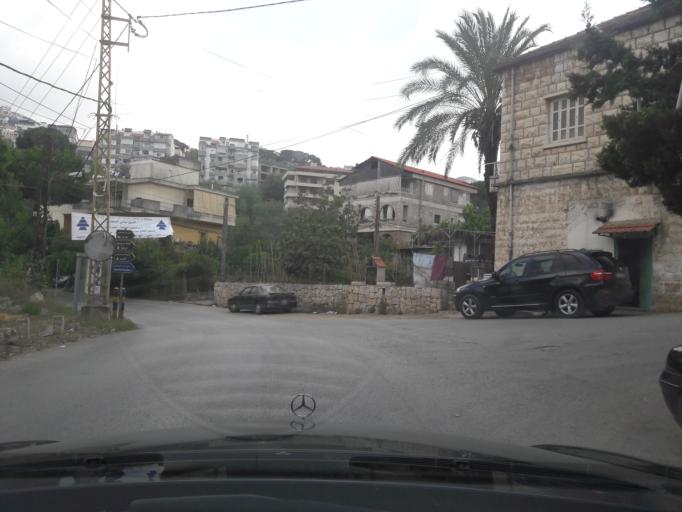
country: LB
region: Mont-Liban
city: Djounie
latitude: 33.9287
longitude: 35.6597
